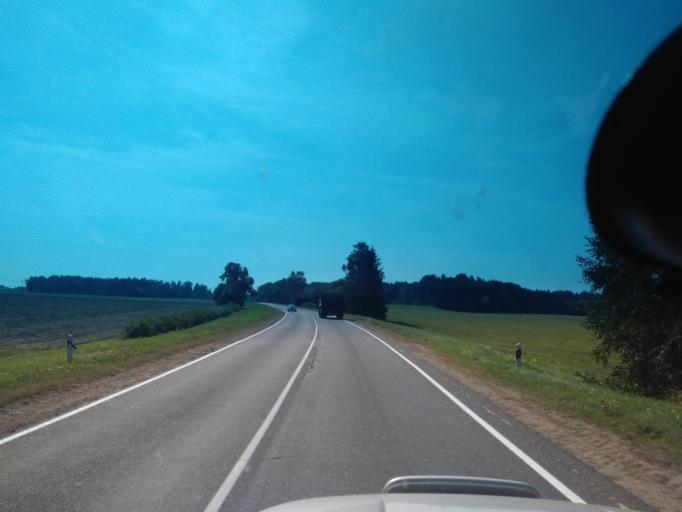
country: BY
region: Minsk
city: Uzda
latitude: 53.3595
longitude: 27.2246
